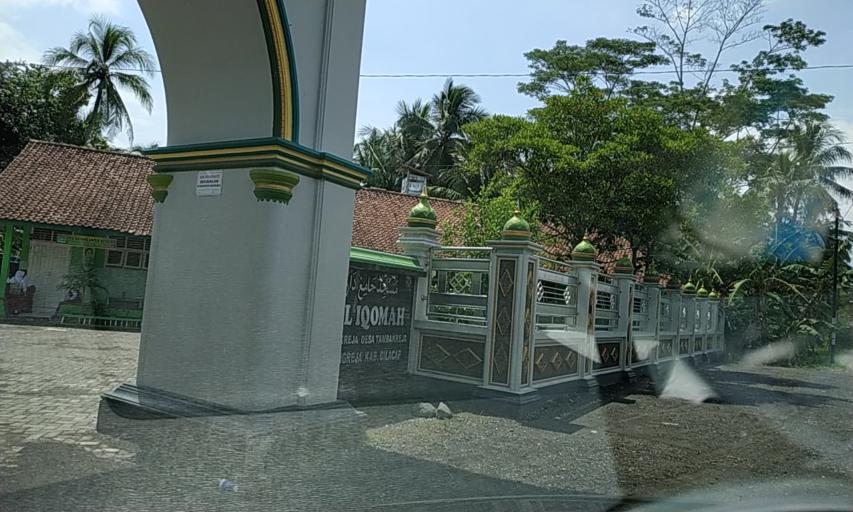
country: ID
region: Central Java
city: Kedungbulu
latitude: -7.5262
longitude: 108.7838
